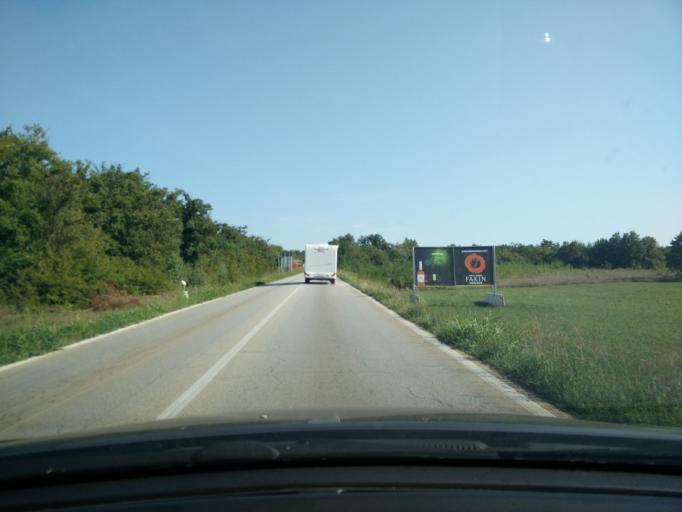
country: HR
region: Istarska
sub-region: Grad Porec
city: Porec
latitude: 45.2788
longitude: 13.6184
